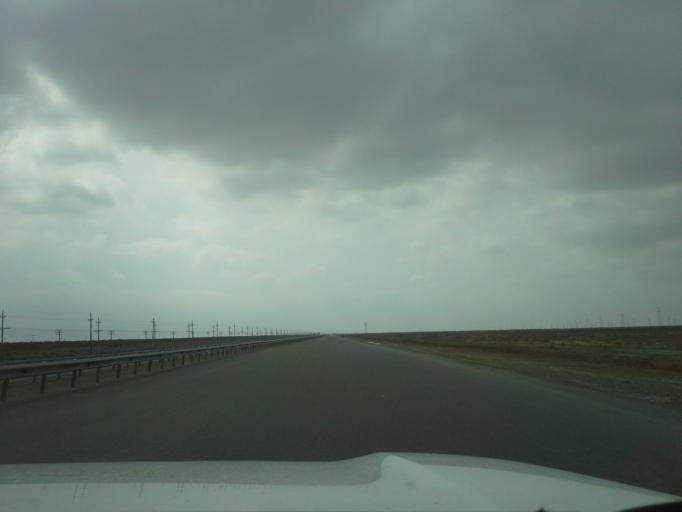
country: IR
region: Razavi Khorasan
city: Kalat-e Naderi
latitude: 37.2125
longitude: 60.0811
